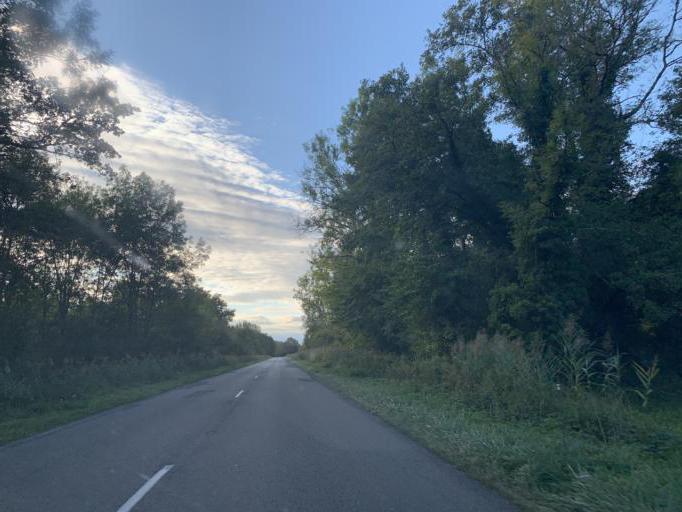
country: FR
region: Rhone-Alpes
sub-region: Departement de l'Isere
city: Les Avenieres
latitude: 45.6821
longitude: 5.6010
